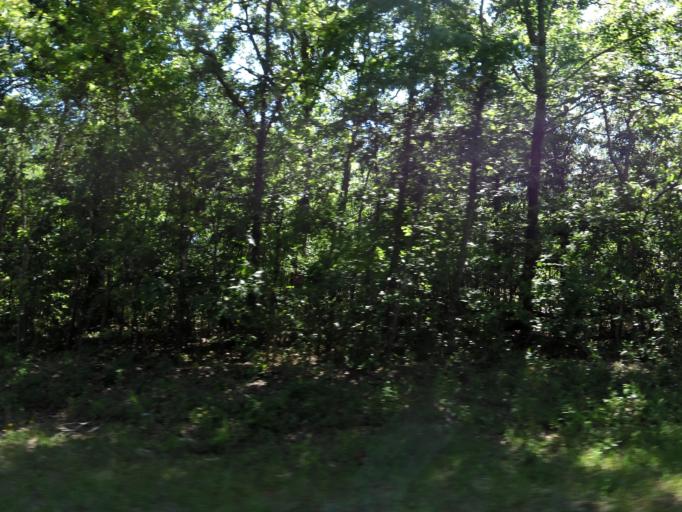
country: US
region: South Carolina
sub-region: Barnwell County
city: Williston
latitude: 33.4998
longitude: -81.5331
